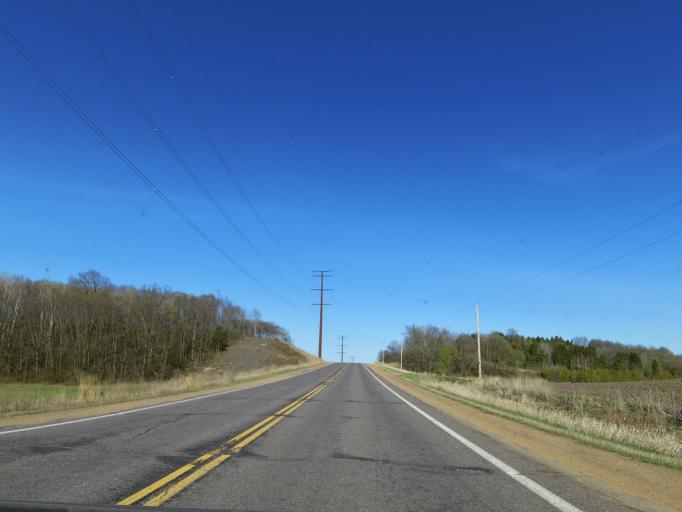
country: US
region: Minnesota
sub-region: Rice County
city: Lonsdale
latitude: 44.5726
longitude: -93.4536
